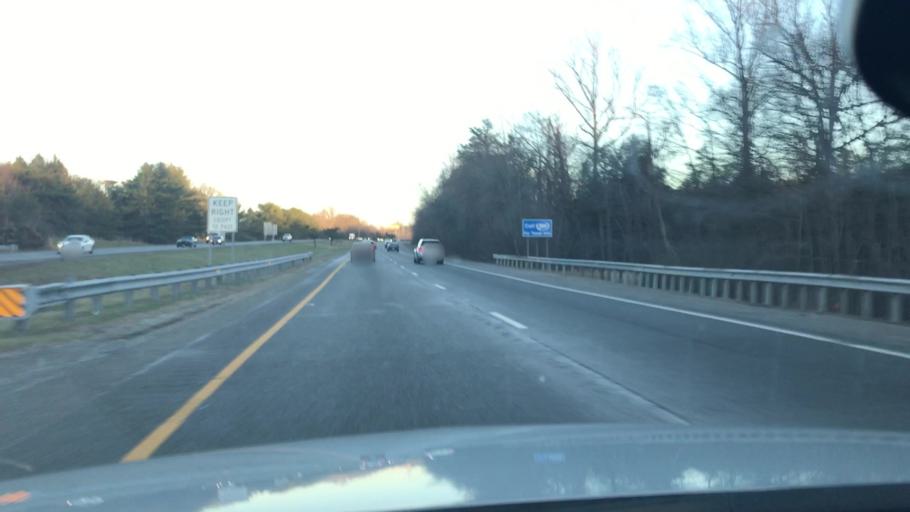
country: US
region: New Jersey
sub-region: Gloucester County
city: Turnersville
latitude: 39.7555
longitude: -75.0353
